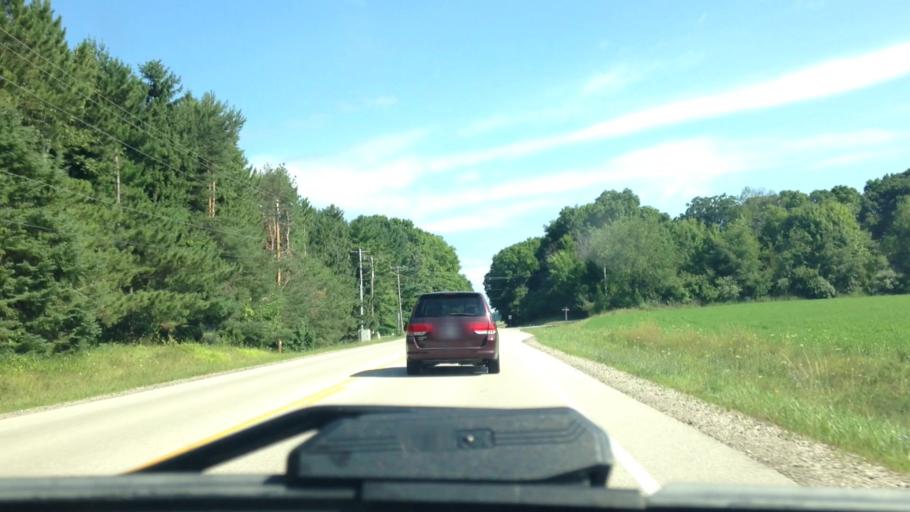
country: US
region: Wisconsin
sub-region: Washington County
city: West Bend
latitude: 43.3970
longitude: -88.2409
